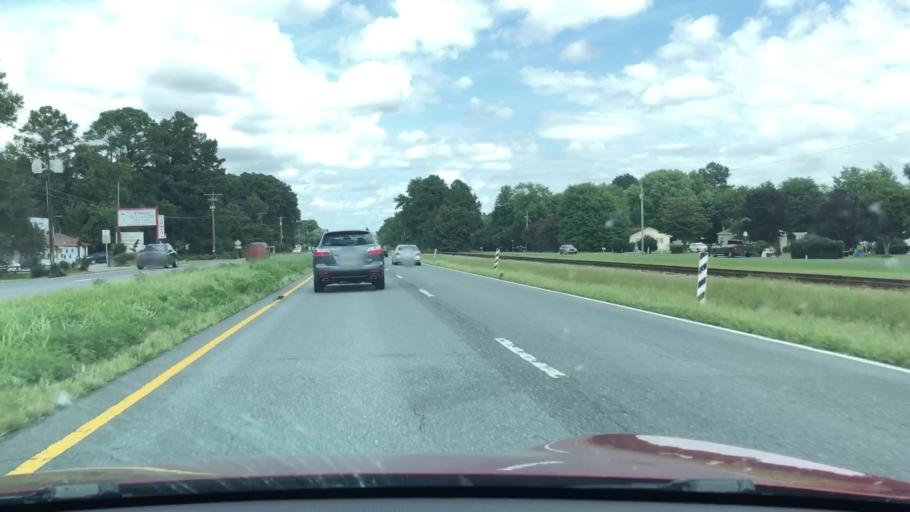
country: US
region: Virginia
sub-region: Accomack County
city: Onancock
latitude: 37.6659
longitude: -75.7318
